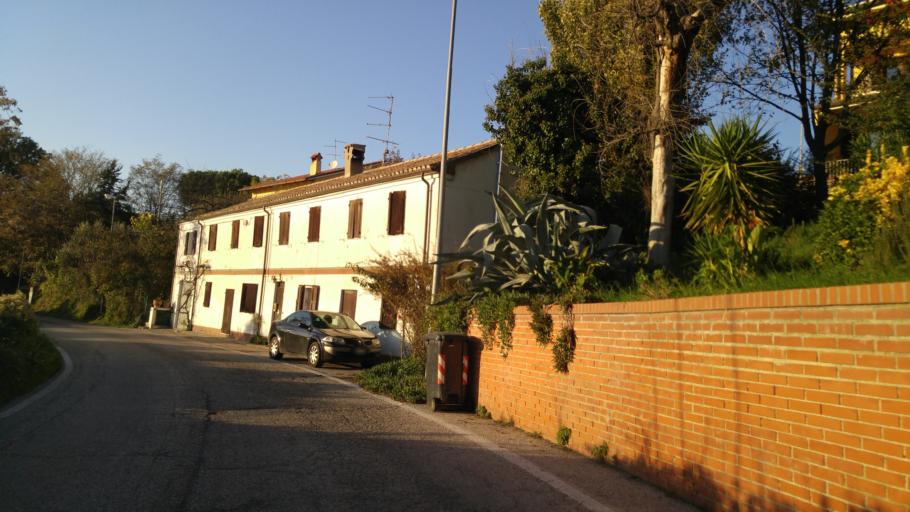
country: IT
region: The Marches
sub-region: Provincia di Pesaro e Urbino
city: Pesaro
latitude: 43.8592
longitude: 12.8857
